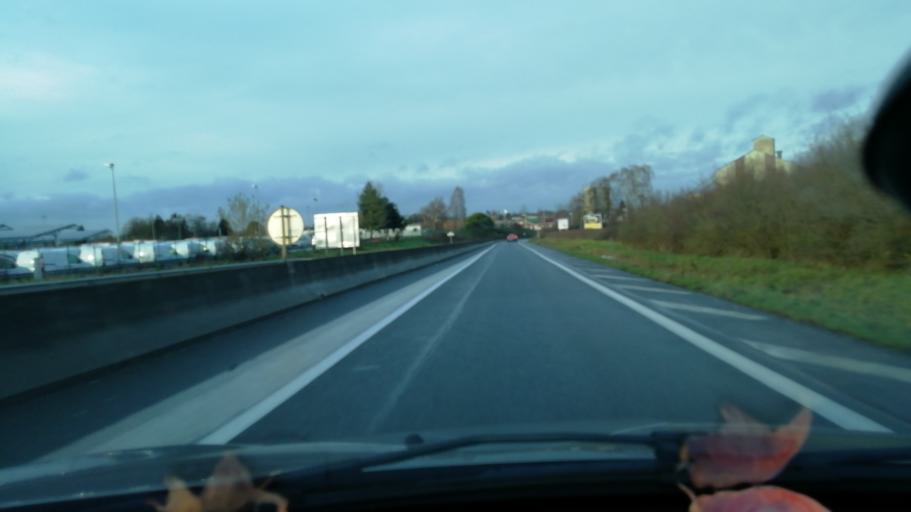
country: FR
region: Nord-Pas-de-Calais
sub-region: Departement du Nord
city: Feignies
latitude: 50.2768
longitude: 3.9218
